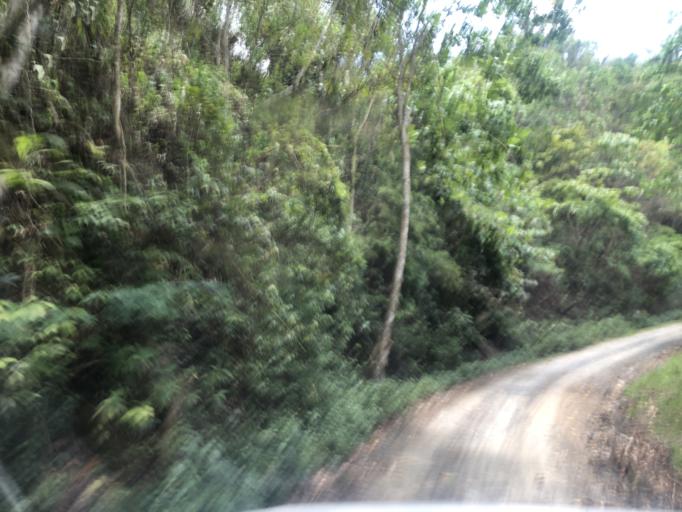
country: LA
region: Phongsali
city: Phongsali
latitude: 21.4479
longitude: 102.1634
